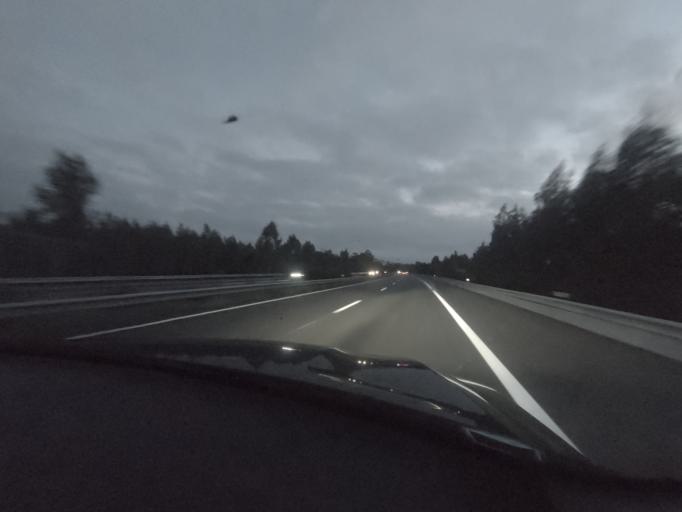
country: PT
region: Leiria
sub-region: Pombal
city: Pombal
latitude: 39.8970
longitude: -8.6903
